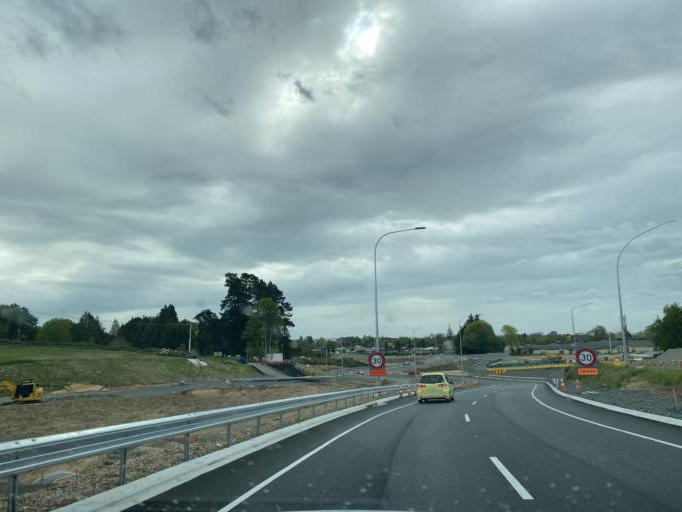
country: NZ
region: Waikato
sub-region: Hamilton City
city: Hamilton
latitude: -37.8027
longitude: 175.3120
